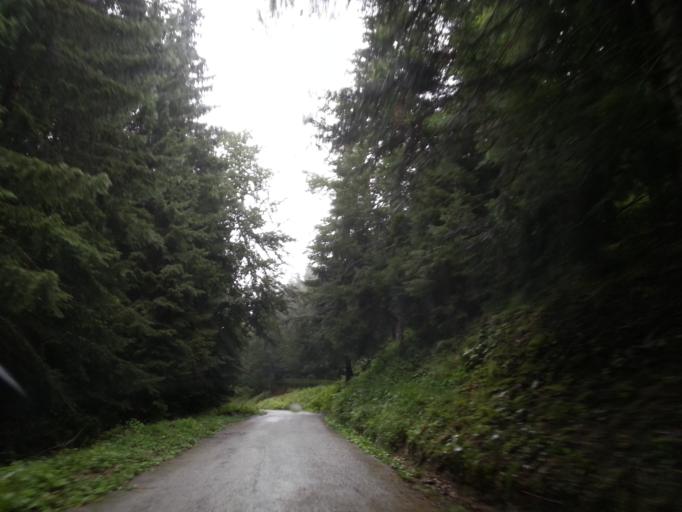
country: FR
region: Rhone-Alpes
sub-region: Departement de la Savoie
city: Marthod
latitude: 45.6991
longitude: 6.4492
